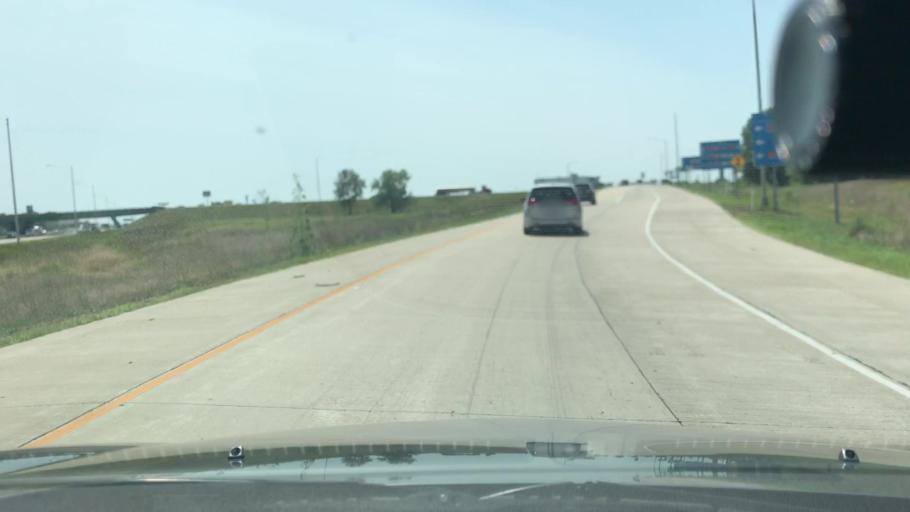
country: US
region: Illinois
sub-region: Jefferson County
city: Mount Vernon
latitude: 38.3156
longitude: -88.9537
